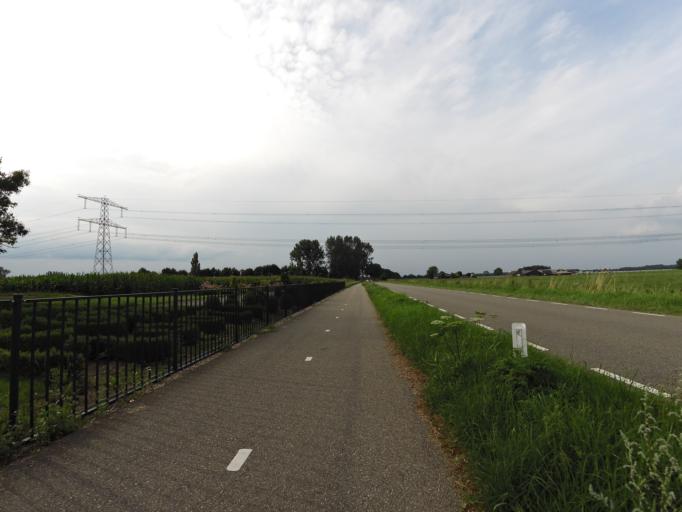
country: NL
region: Gelderland
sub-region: Gemeente Doesburg
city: Doesburg
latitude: 51.9698
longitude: 6.1355
